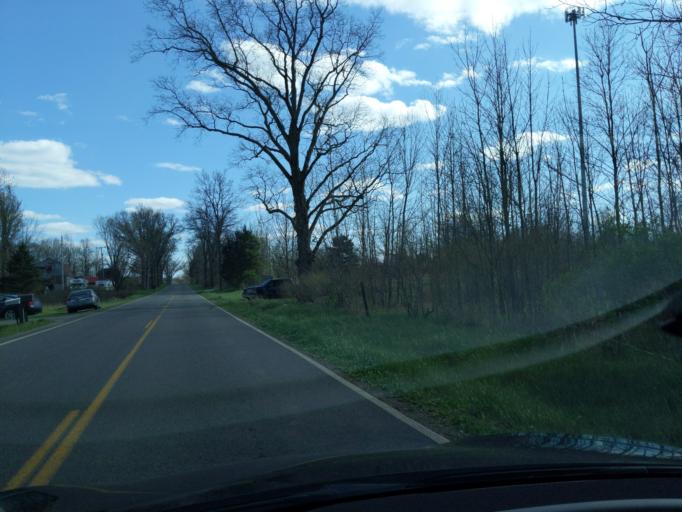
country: US
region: Michigan
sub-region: Ingham County
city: Leslie
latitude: 42.3842
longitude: -84.5416
